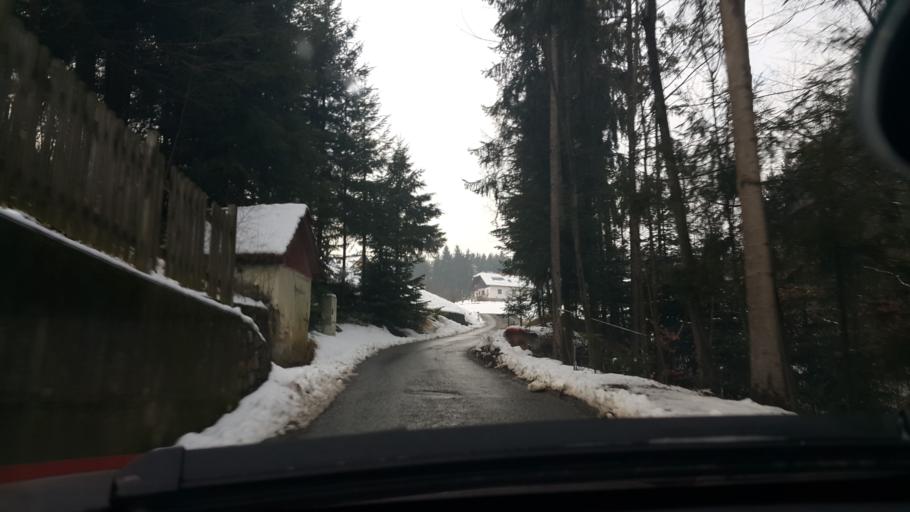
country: AT
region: Styria
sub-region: Politischer Bezirk Graz-Umgebung
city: Sankt Oswald bei Plankenwarth
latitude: 47.0877
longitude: 15.2511
